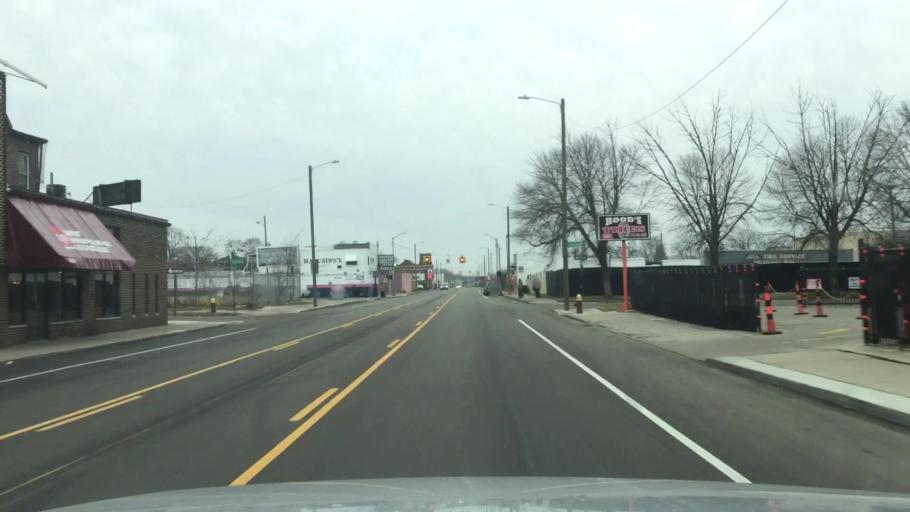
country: US
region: Michigan
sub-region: Wayne County
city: Grosse Pointe Park
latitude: 42.3753
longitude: -82.9872
